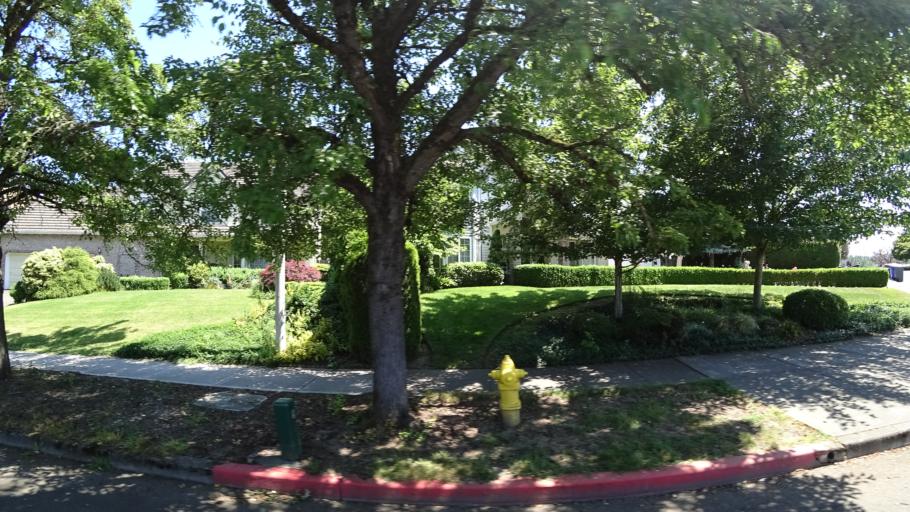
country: US
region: Oregon
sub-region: Multnomah County
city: Fairview
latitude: 45.5533
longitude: -122.4395
